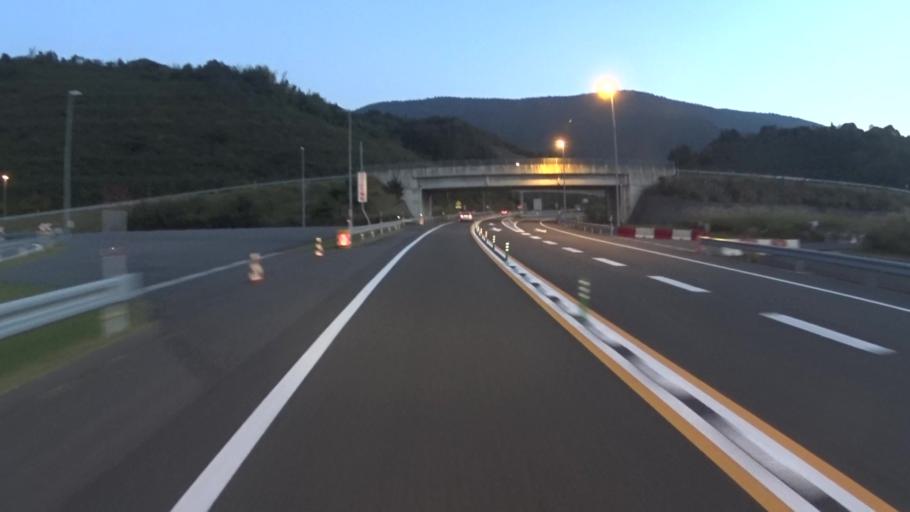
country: JP
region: Kyoto
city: Miyazu
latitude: 35.5156
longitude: 135.1924
